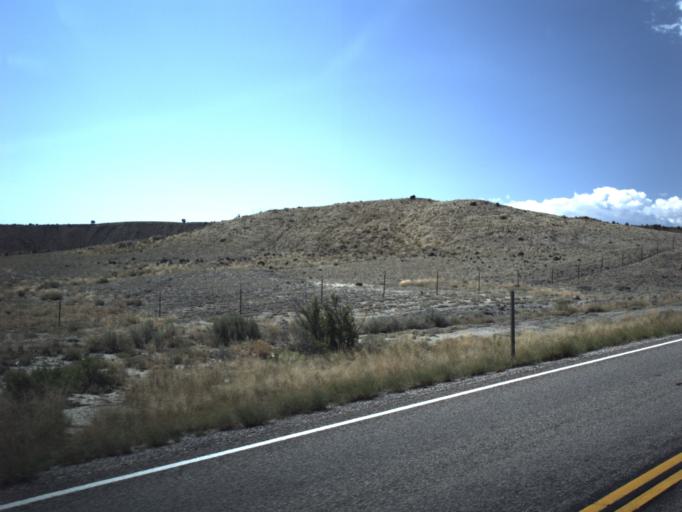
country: US
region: Utah
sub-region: Emery County
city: Ferron
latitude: 38.7995
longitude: -111.3424
